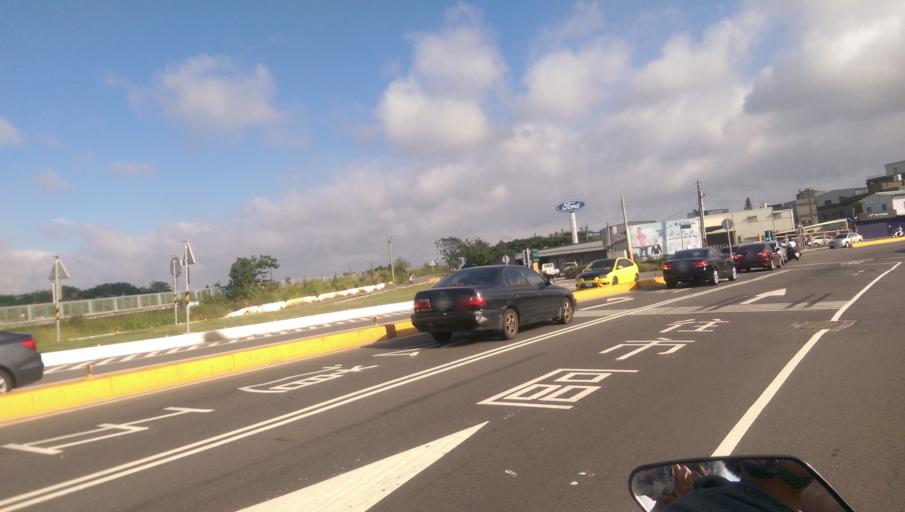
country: TW
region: Taiwan
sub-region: Hsinchu
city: Hsinchu
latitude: 24.8316
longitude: 120.9550
